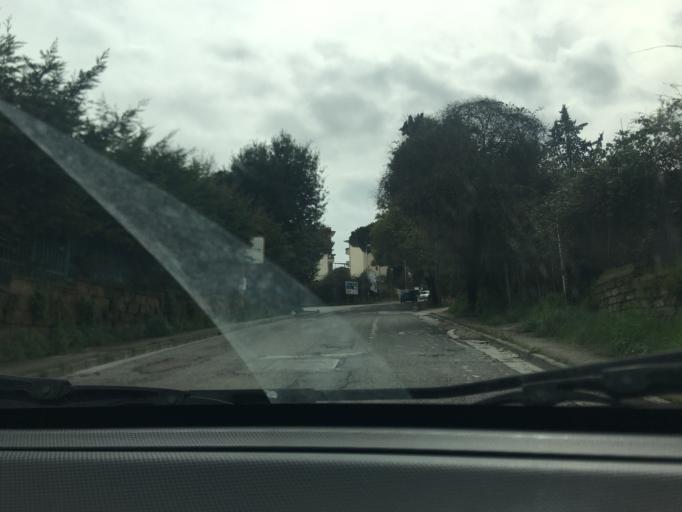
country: IT
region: Campania
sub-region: Provincia di Napoli
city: Marano di Napoli
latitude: 40.8938
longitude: 14.1812
